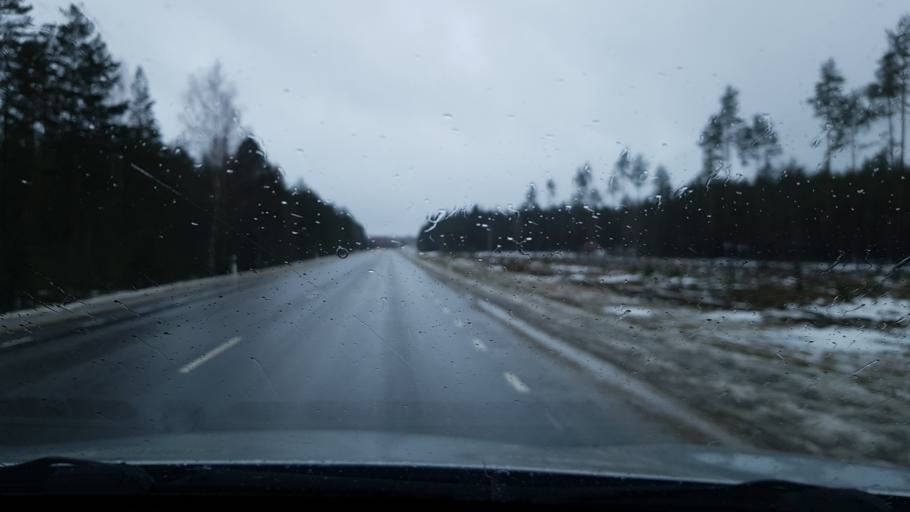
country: EE
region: Vorumaa
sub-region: Voru linn
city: Voru
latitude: 57.8025
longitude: 26.9633
